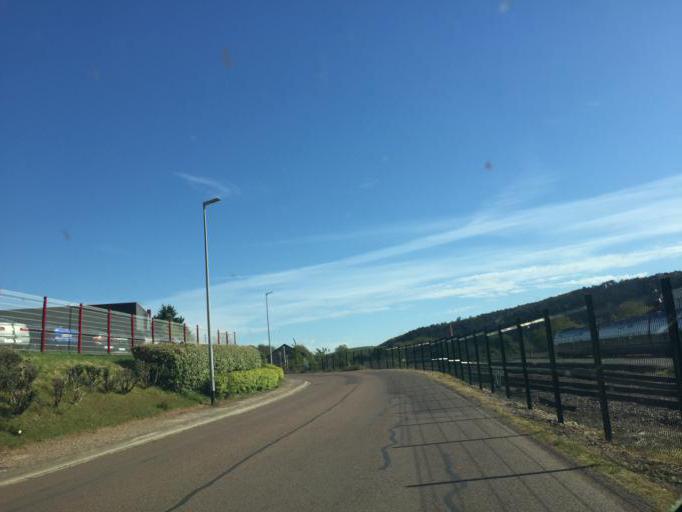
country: FR
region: Bourgogne
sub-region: Departement de la Nievre
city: Clamecy
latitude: 47.4662
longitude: 3.5197
